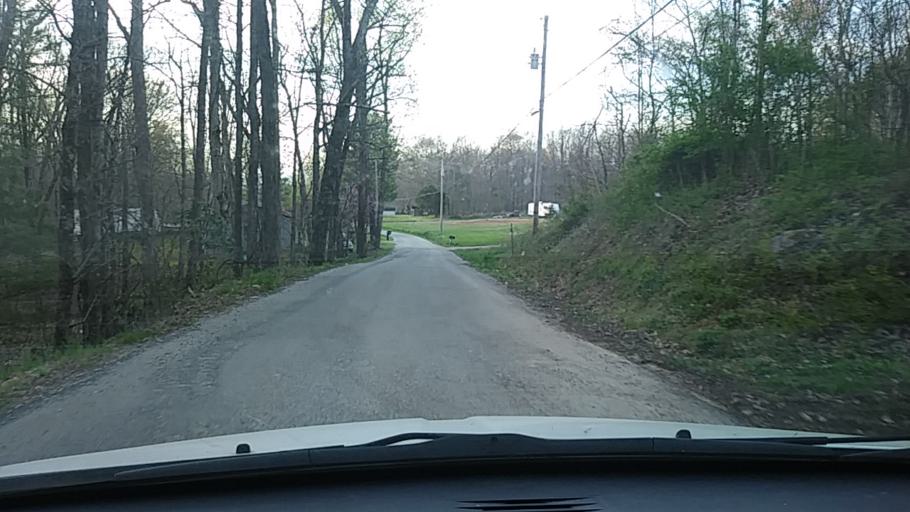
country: US
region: Tennessee
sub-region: Greene County
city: Tusculum
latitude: 36.0912
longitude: -82.6962
